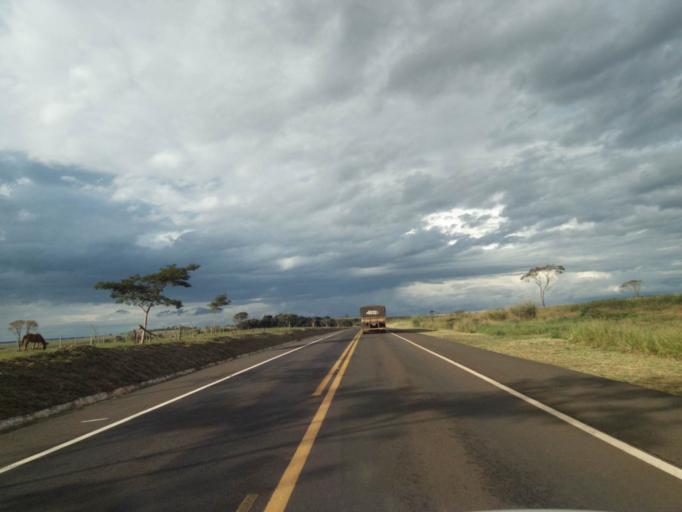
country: PY
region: Canindeyu
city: Salto del Guaira
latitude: -24.0842
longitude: -54.0744
